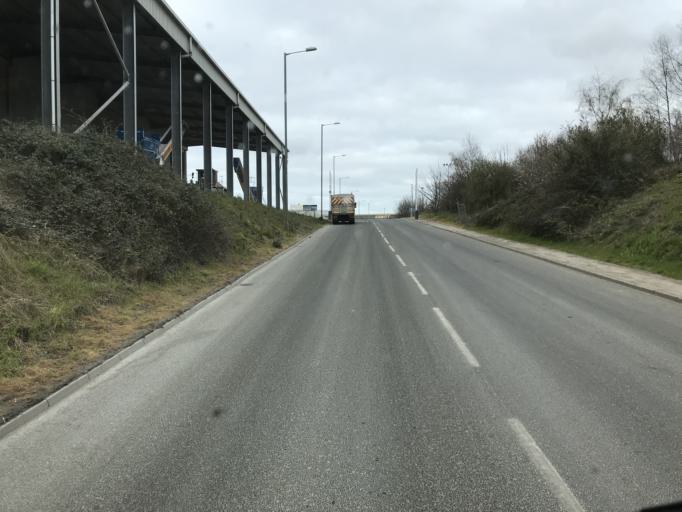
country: GB
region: England
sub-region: Cheshire West and Chester
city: Ellesmere Port
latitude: 53.3511
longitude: -2.9044
